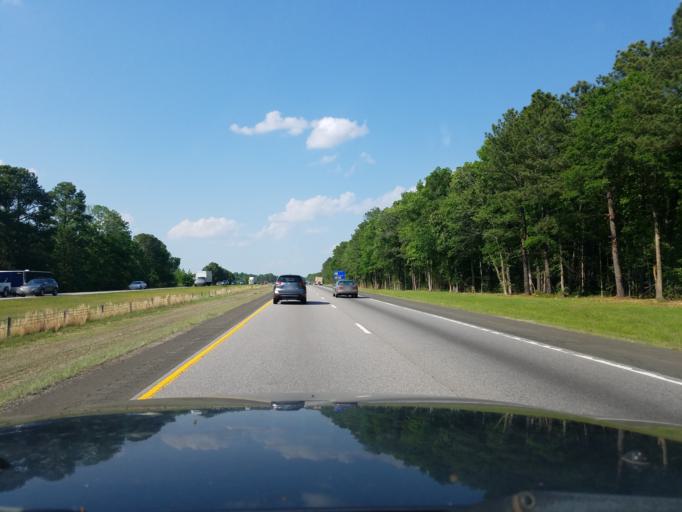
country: US
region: North Carolina
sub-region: Granville County
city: Butner
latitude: 36.1130
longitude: -78.7496
